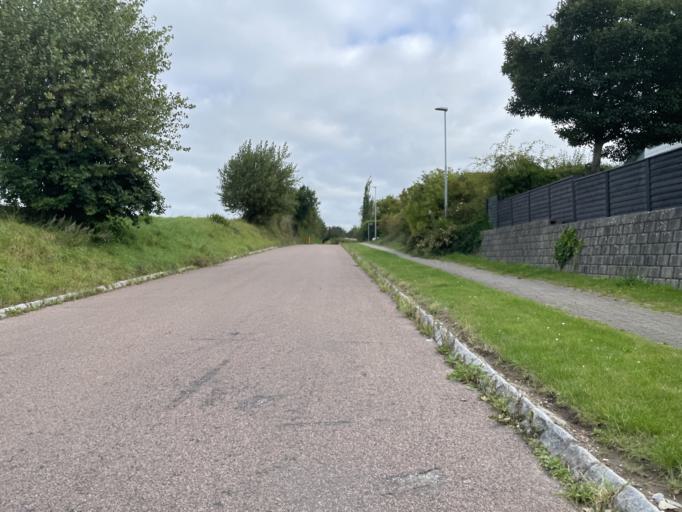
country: DK
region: South Denmark
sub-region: Kerteminde Kommune
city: Kerteminde
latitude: 55.4567
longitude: 10.6302
